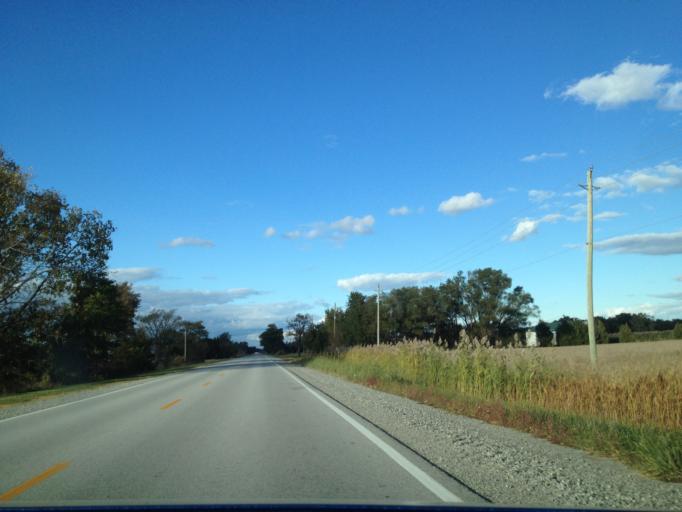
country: US
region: Michigan
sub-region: Wayne County
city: Grosse Pointe
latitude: 42.1426
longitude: -82.7331
